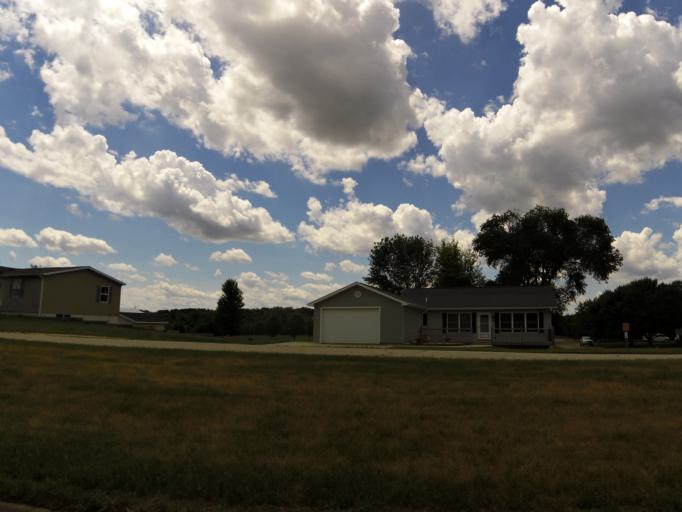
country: US
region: Iowa
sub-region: Fayette County
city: Oelwein
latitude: 42.6129
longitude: -91.9045
